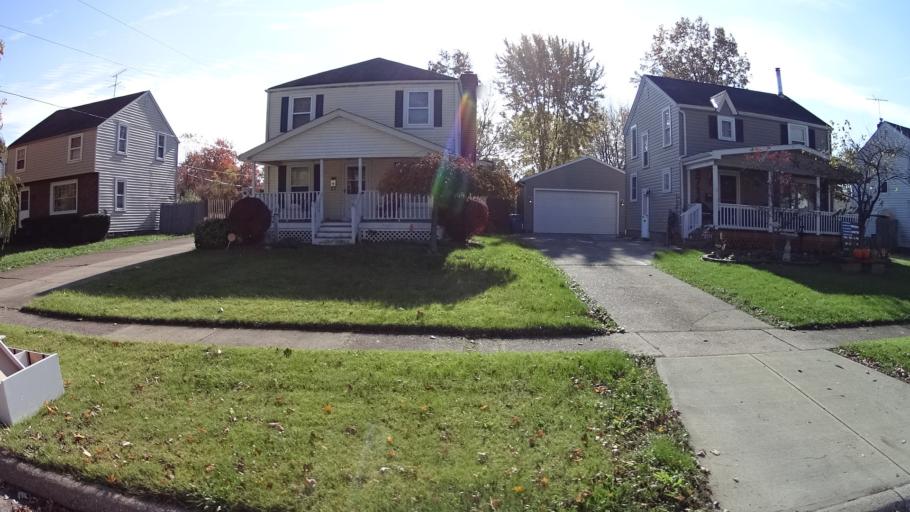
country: US
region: Ohio
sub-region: Lorain County
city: Sheffield Lake
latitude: 41.4763
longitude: -82.1430
